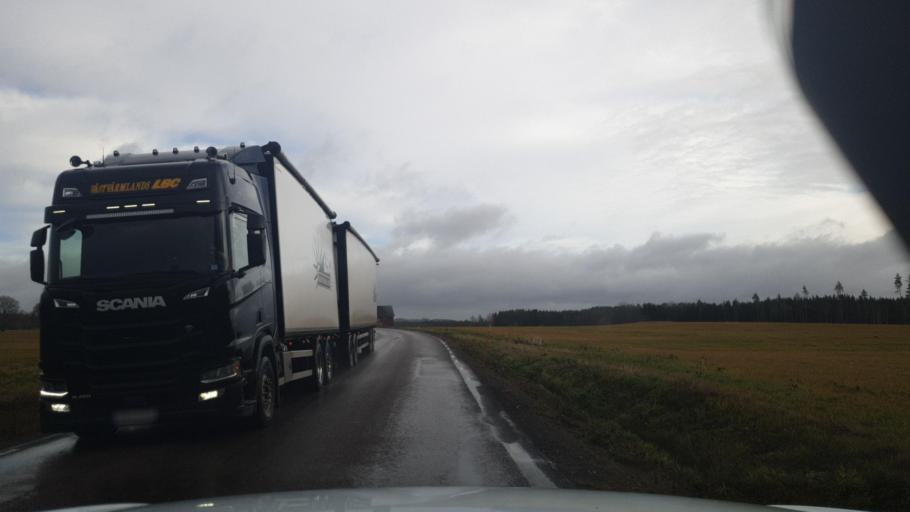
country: SE
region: Vaermland
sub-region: Eda Kommun
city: Charlottenberg
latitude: 59.7780
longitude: 12.1688
